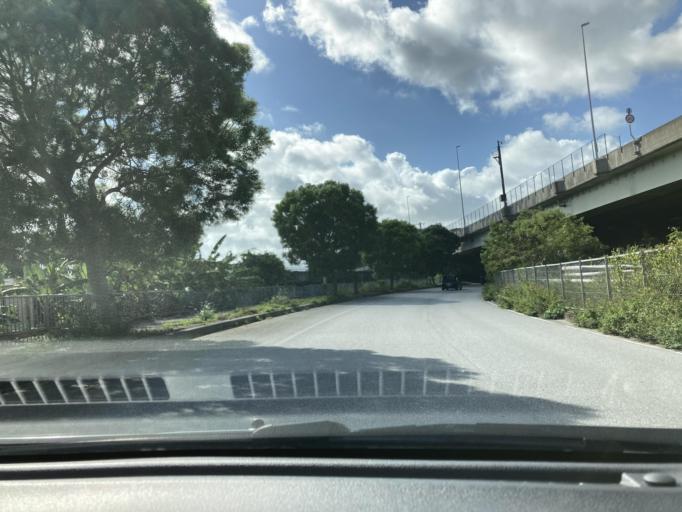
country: JP
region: Okinawa
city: Tomigusuku
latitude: 26.1809
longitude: 127.7210
